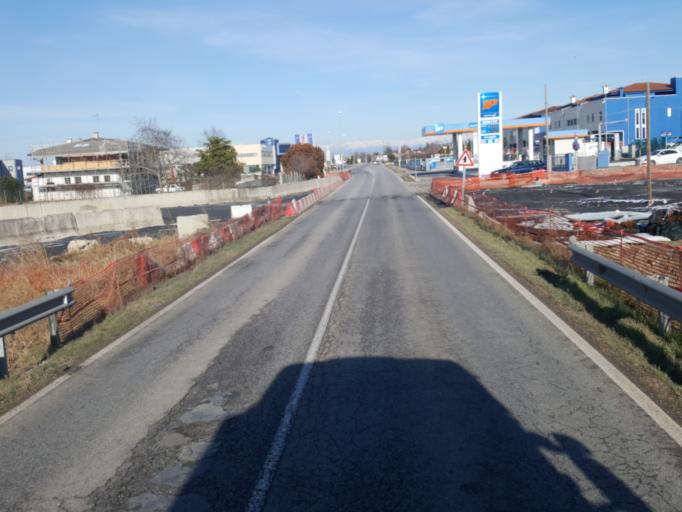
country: IT
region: Friuli Venezia Giulia
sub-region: Provincia di Udine
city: Porpetto
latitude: 45.8470
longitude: 13.2124
